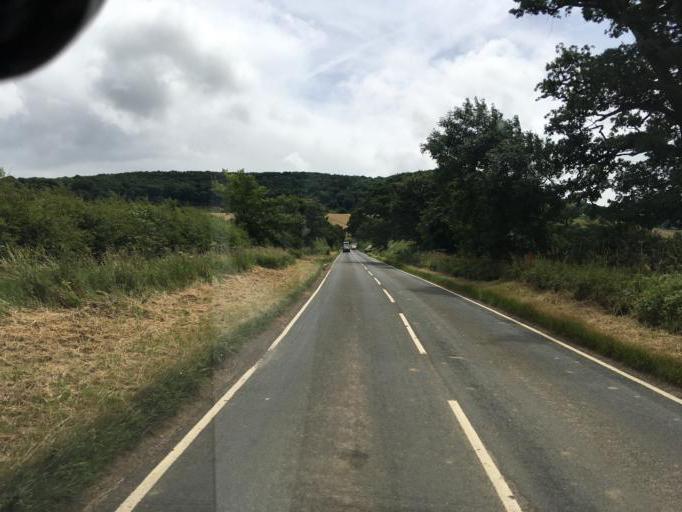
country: GB
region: England
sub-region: Gloucestershire
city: Stonehouse
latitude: 51.7216
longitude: -2.3073
